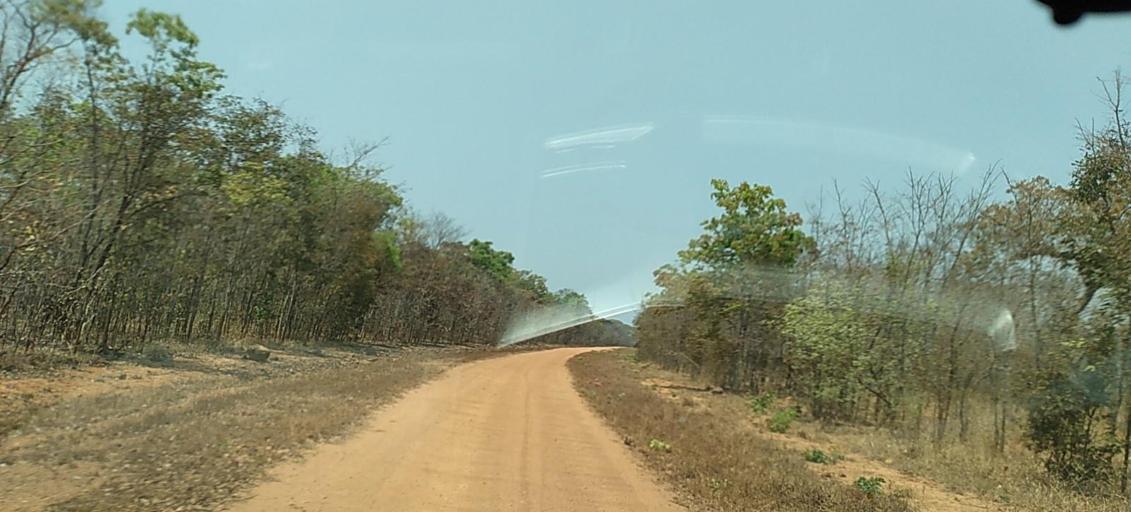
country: ZM
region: Central
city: Mumbwa
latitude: -14.3869
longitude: 26.4868
